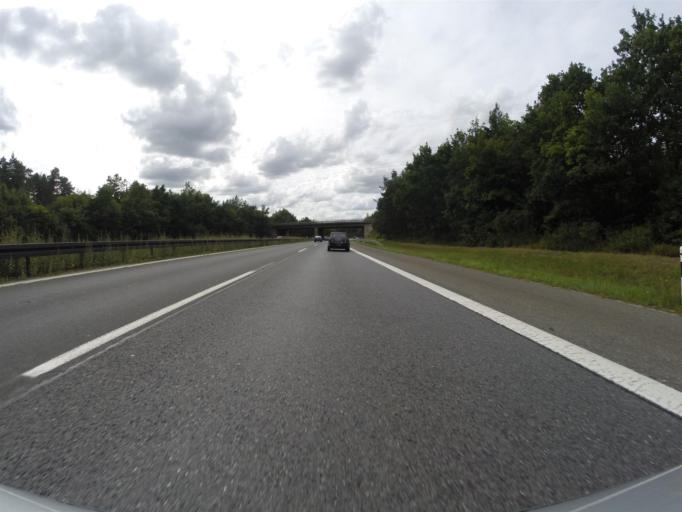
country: DE
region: Bavaria
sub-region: Regierungsbezirk Mittelfranken
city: Nuernberg
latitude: 49.3948
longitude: 11.0856
